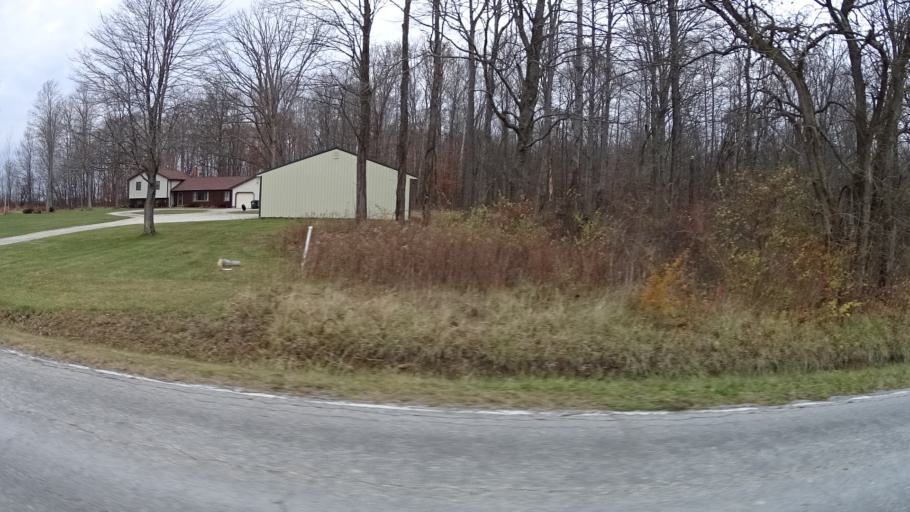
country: US
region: Ohio
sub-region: Lorain County
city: Lagrange
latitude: 41.1364
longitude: -82.0833
